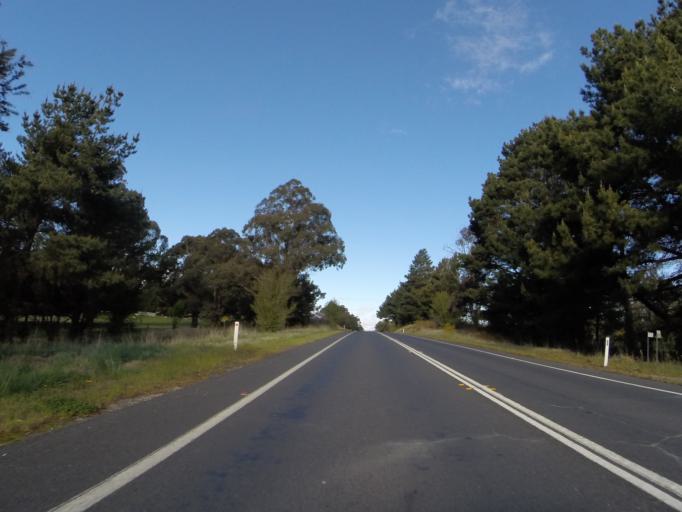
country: AU
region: New South Wales
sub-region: Wingecarribee
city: Moss Vale
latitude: -34.5668
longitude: 150.4219
